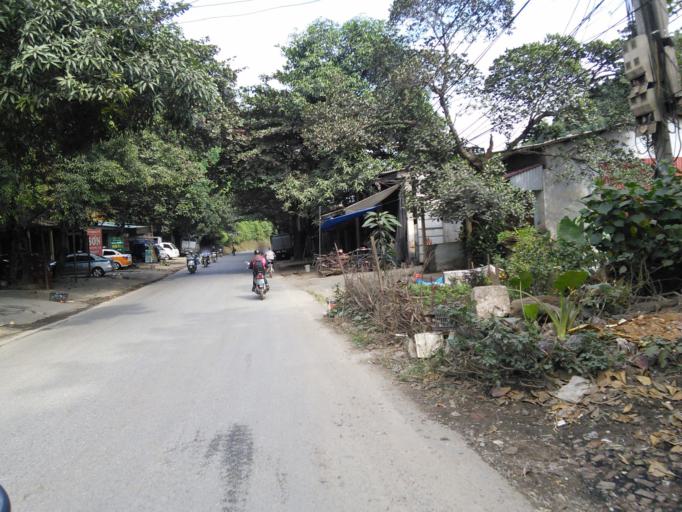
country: VN
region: Lao Cai
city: Lao Cai
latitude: 22.4727
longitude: 103.9703
